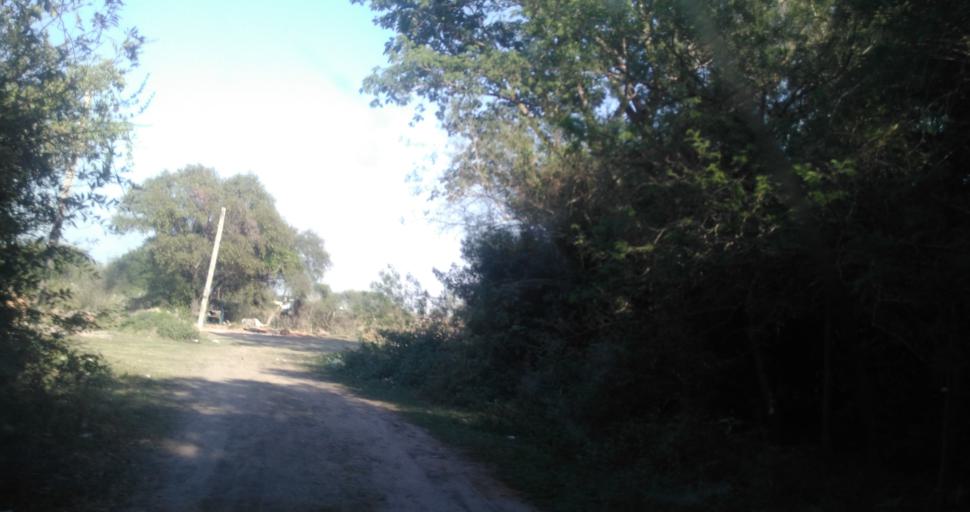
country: AR
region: Chaco
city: Fontana
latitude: -27.4248
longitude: -59.0361
